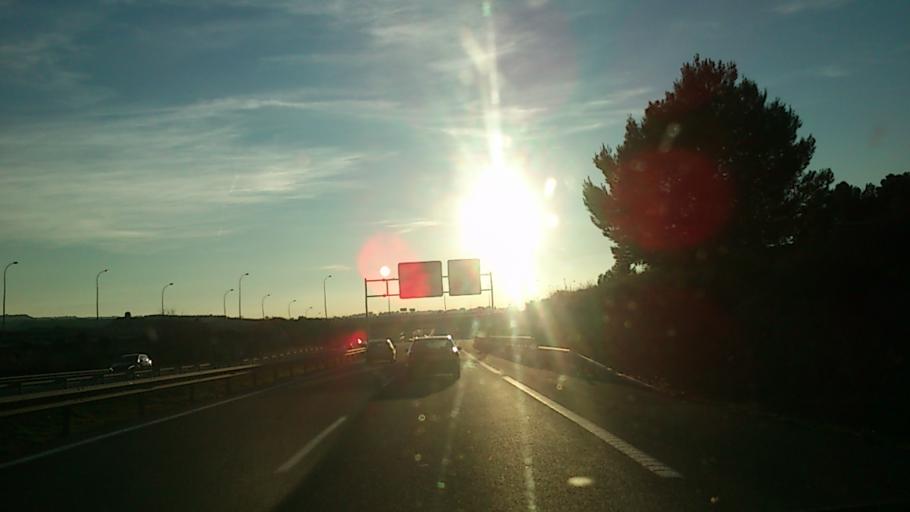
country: ES
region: Castille-La Mancha
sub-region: Provincia de Guadalajara
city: Tortola de Henares
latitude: 40.6647
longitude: -3.1106
